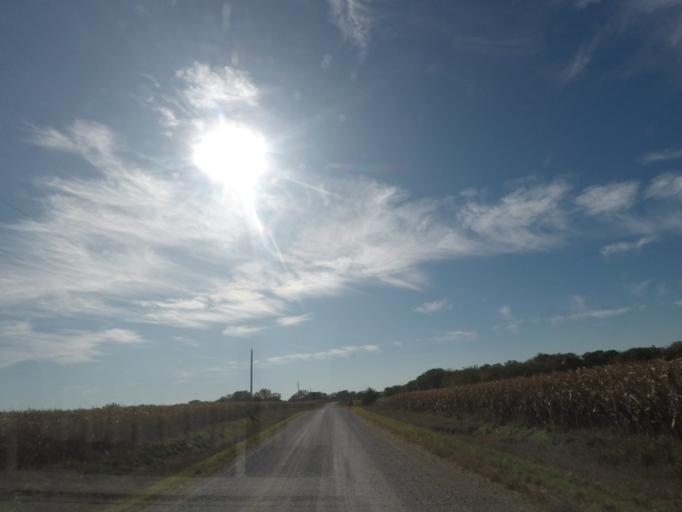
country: US
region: Iowa
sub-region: Story County
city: Nevada
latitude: 42.0763
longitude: -93.3504
